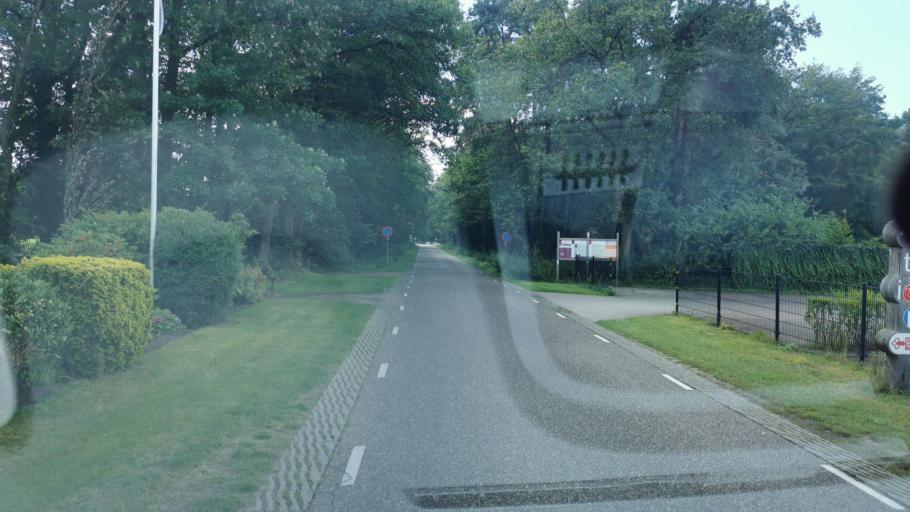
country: NL
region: Overijssel
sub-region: Gemeente Losser
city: Losser
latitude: 52.2809
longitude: 7.0200
